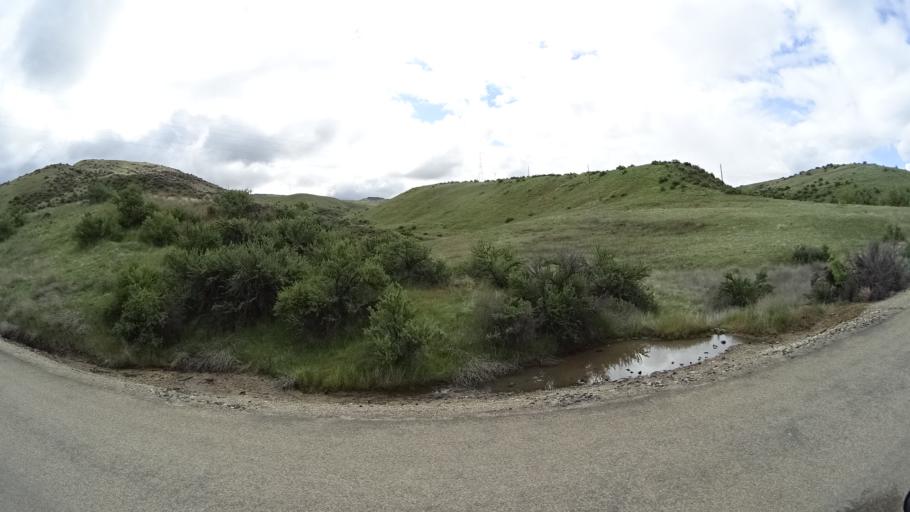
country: US
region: Idaho
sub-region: Ada County
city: Garden City
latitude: 43.7280
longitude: -116.2332
